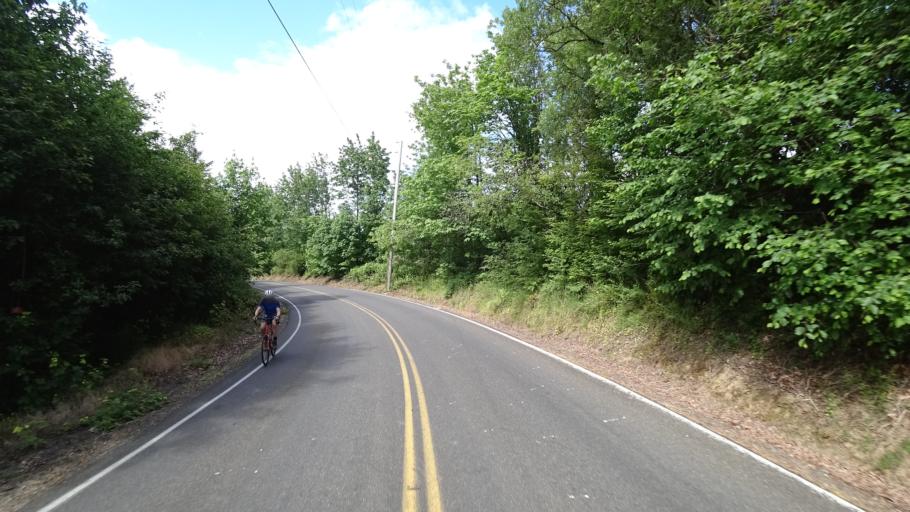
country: US
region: Oregon
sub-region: Washington County
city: Bethany
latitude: 45.6119
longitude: -122.8177
